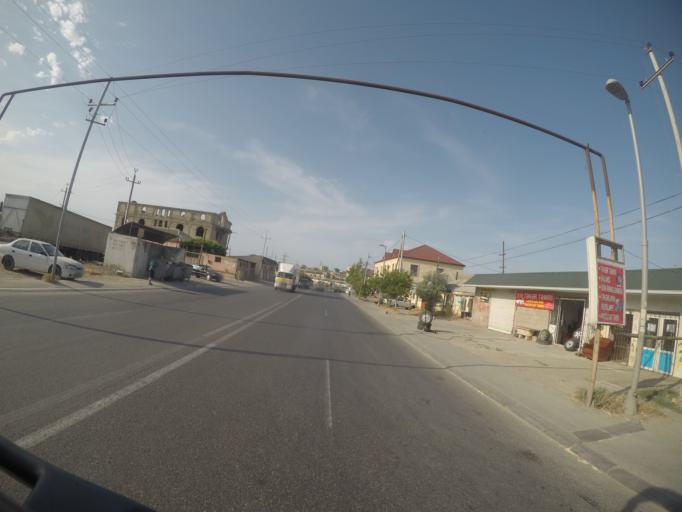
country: AZ
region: Baki
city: Binagadi
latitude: 40.4779
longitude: 49.8338
